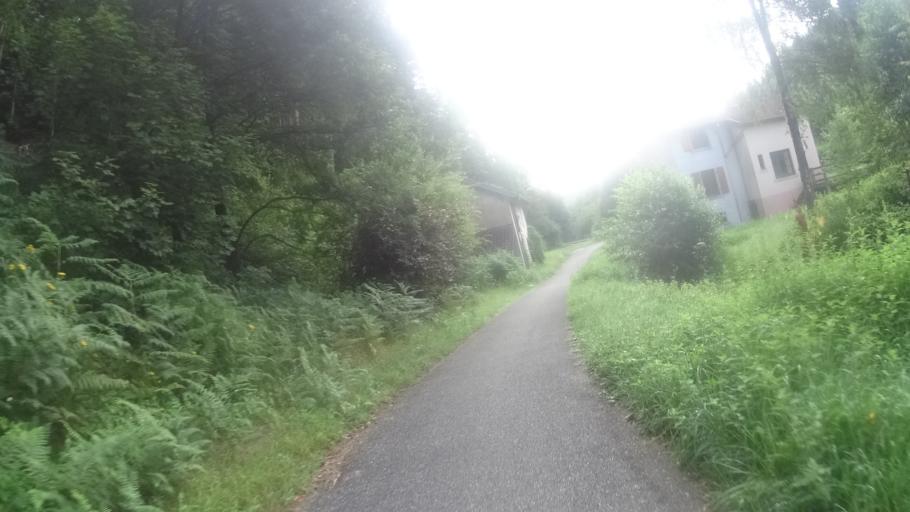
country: FR
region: Lorraine
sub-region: Departement de la Moselle
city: Phalsbourg
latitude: 48.7278
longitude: 7.2328
